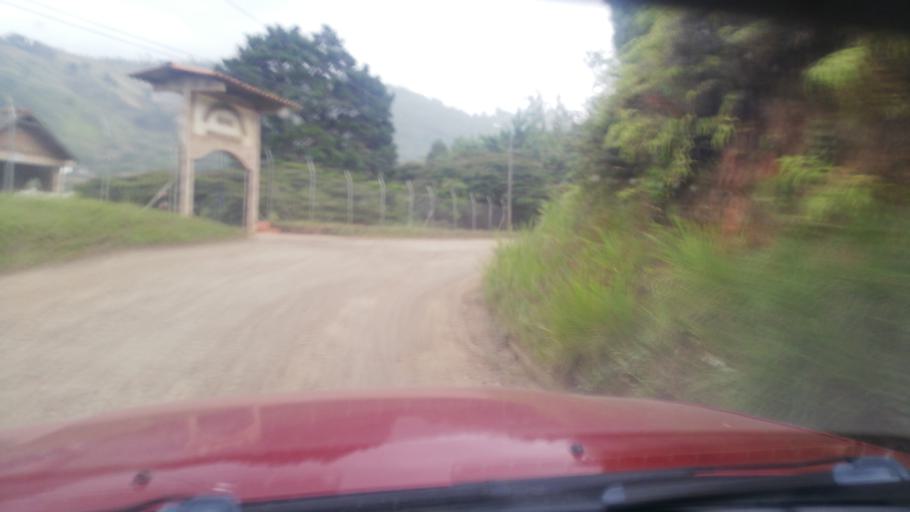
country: CO
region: Valle del Cauca
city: Cali
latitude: 3.4941
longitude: -76.5479
